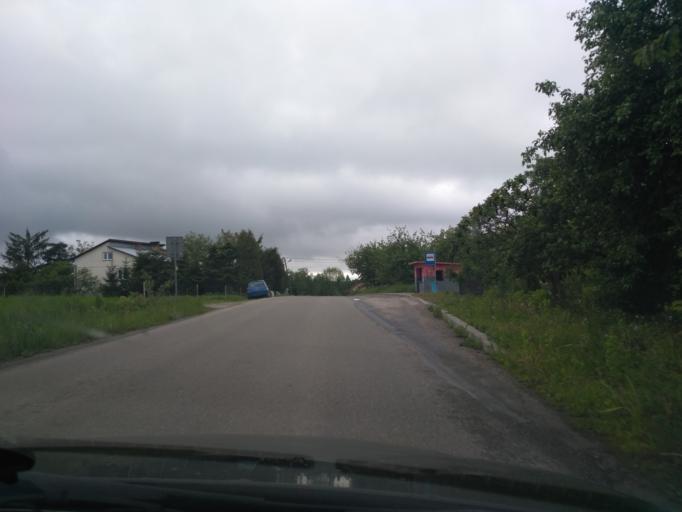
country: PL
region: Subcarpathian Voivodeship
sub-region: Powiat jasielski
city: Jaslo
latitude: 49.8012
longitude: 21.5281
